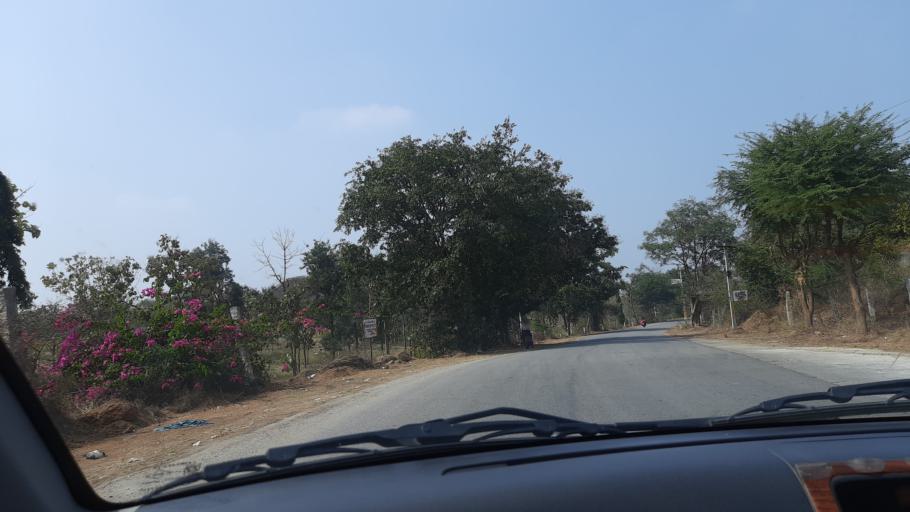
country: IN
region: Telangana
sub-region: Rangareddi
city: Lal Bahadur Nagar
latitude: 17.2749
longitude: 78.6590
